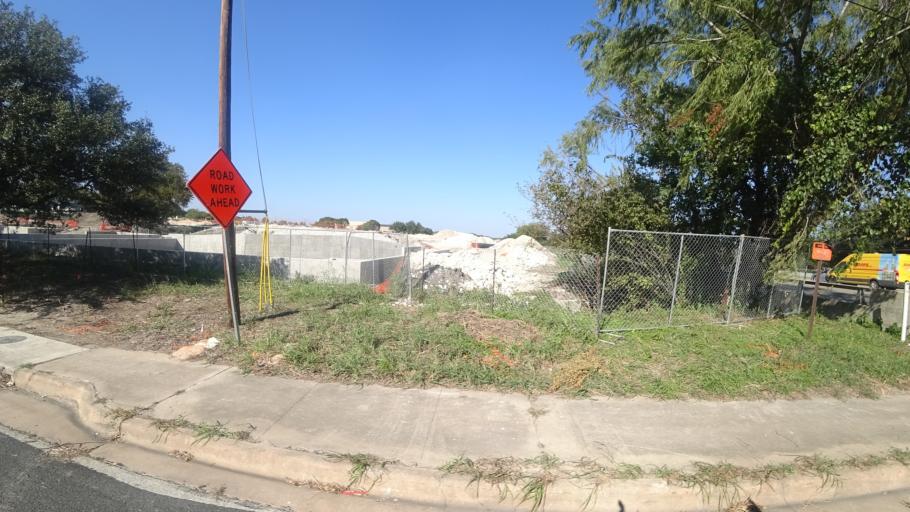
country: US
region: Texas
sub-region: Travis County
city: Austin
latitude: 30.3388
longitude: -97.6825
